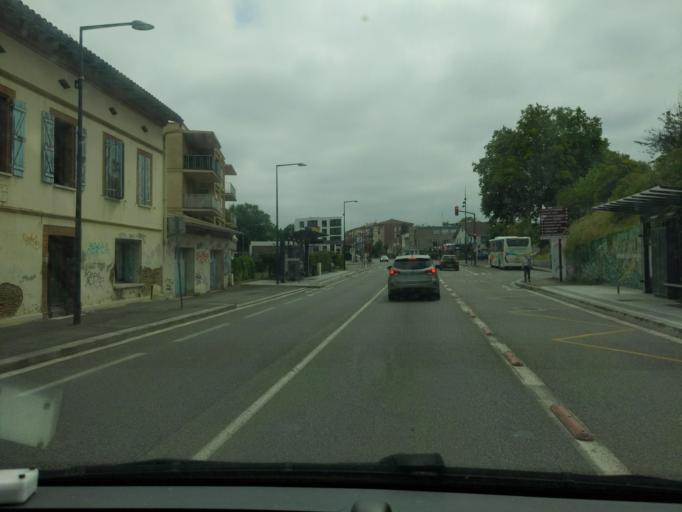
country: FR
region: Midi-Pyrenees
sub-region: Departement de la Haute-Garonne
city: Ramonville-Saint-Agne
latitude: 43.5411
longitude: 1.4787
